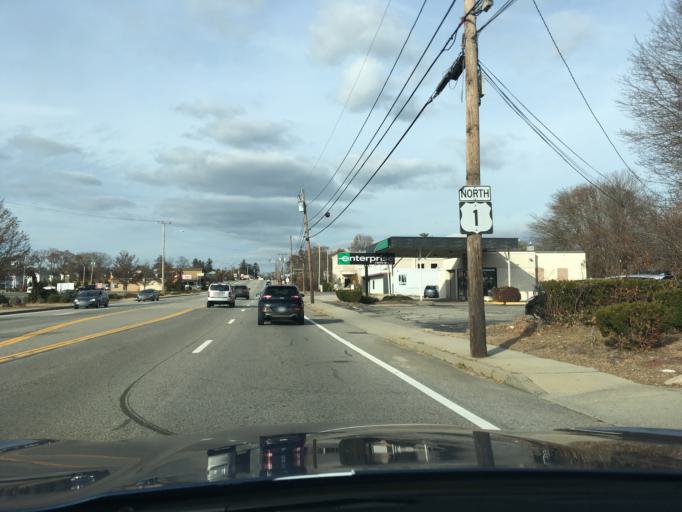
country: US
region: Rhode Island
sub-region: Kent County
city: East Greenwich
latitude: 41.6075
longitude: -71.4558
